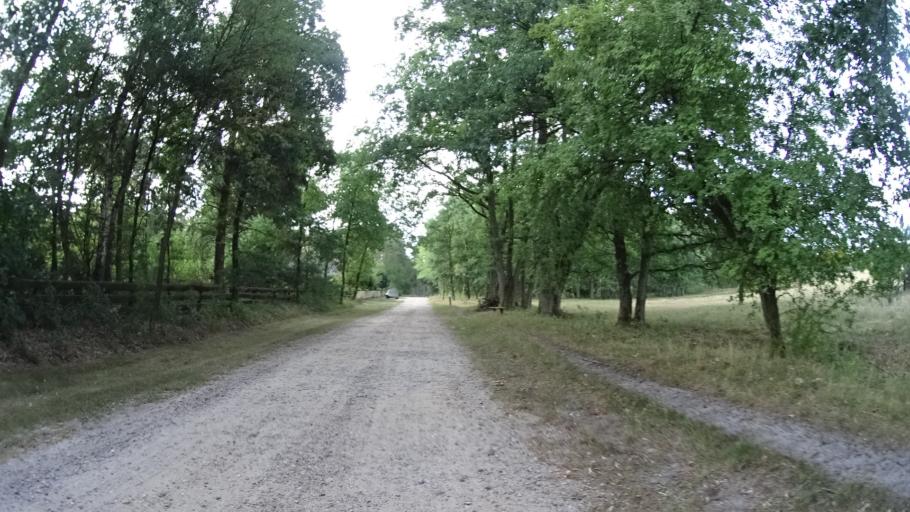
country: DE
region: Lower Saxony
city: Handeloh
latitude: 53.2152
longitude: 9.8804
